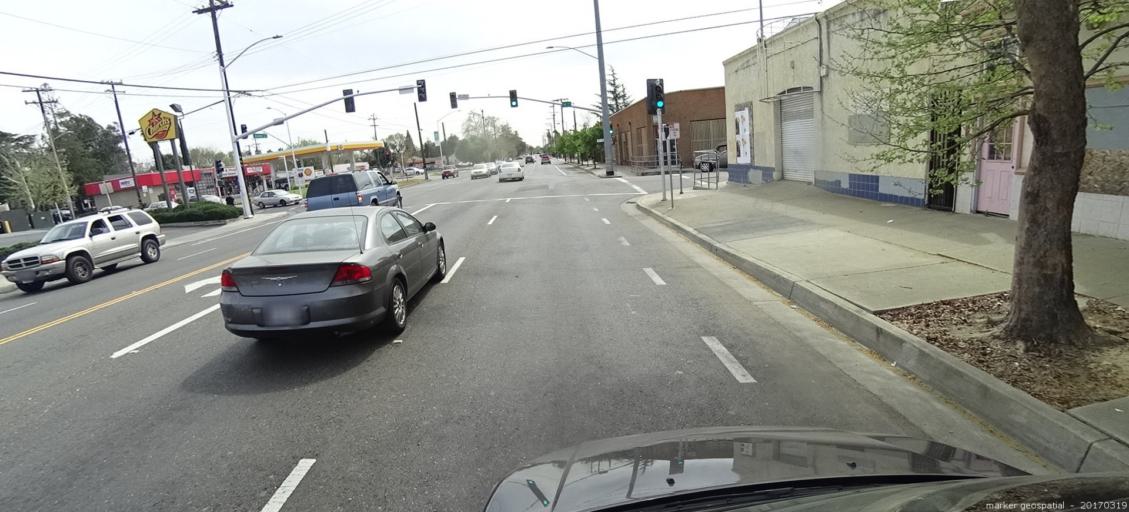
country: US
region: California
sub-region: Sacramento County
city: Parkway
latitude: 38.5398
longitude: -121.4500
